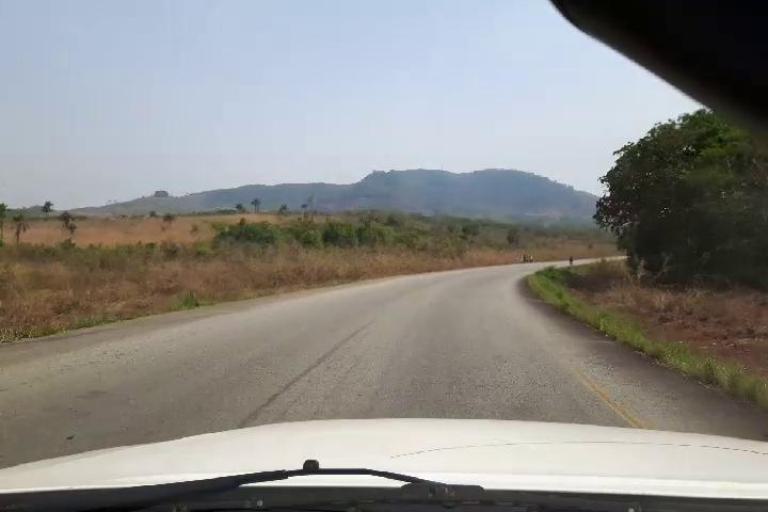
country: SL
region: Northern Province
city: Yonibana
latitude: 8.3832
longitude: -12.1951
